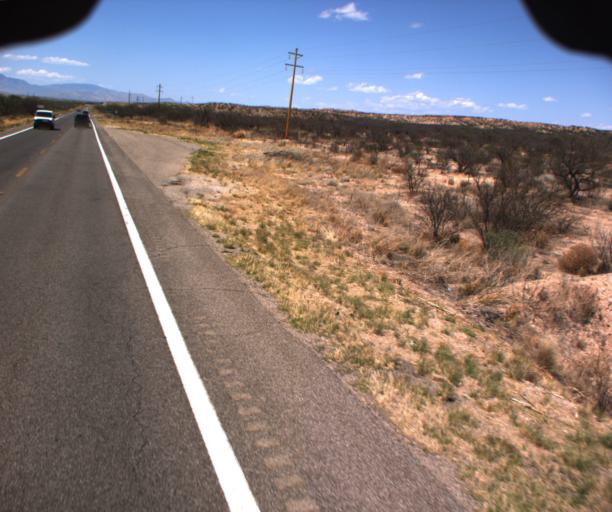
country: US
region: Arizona
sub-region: Cochise County
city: Saint David
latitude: 31.8447
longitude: -110.1934
